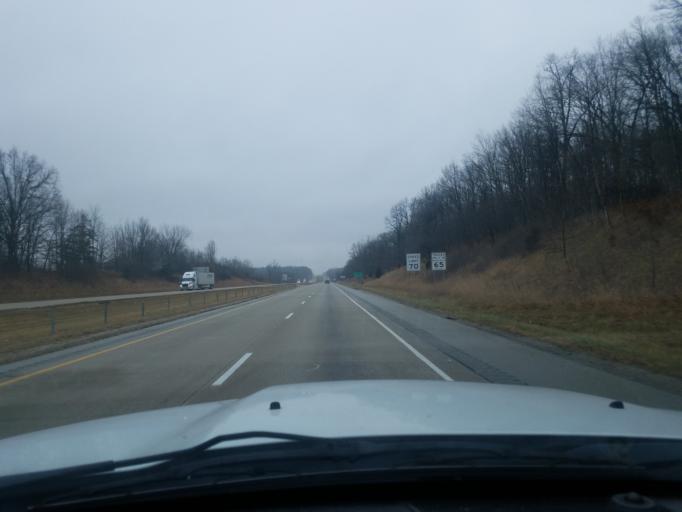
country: US
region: Indiana
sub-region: Grant County
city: Upland
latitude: 40.4885
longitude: -85.5490
